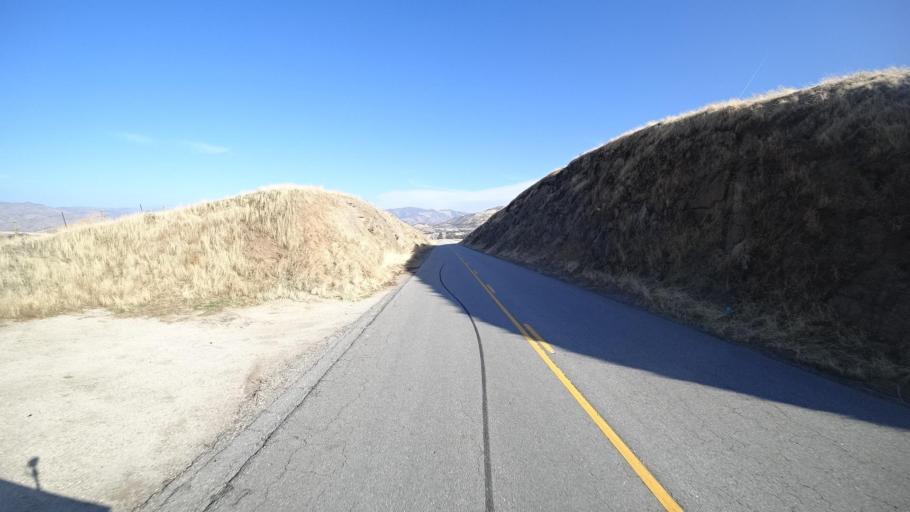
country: US
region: California
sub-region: Kern County
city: Bear Valley Springs
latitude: 35.2642
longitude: -118.6689
